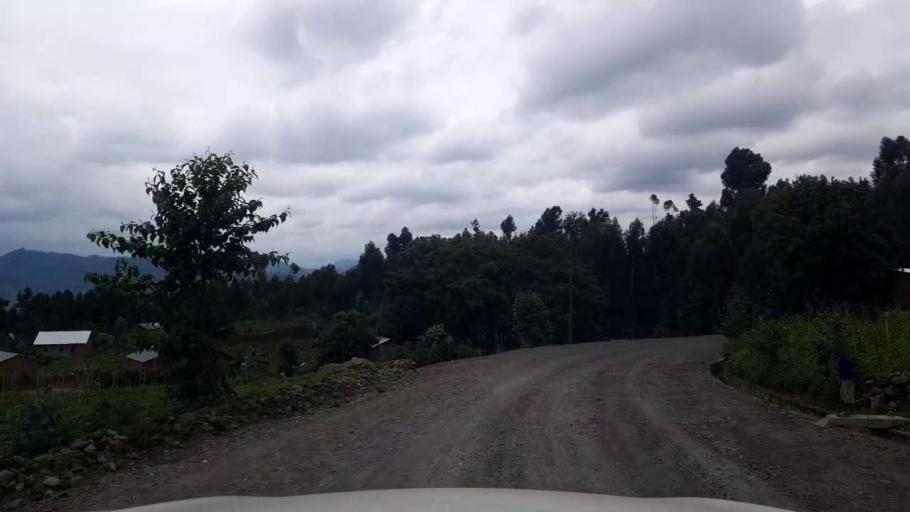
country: RW
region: Northern Province
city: Musanze
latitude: -1.5395
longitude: 29.5344
